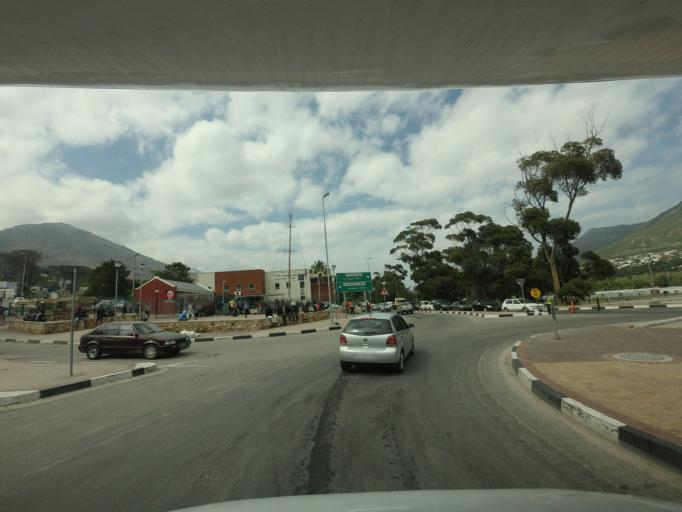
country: ZA
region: Western Cape
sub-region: City of Cape Town
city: Constantia
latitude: -34.0299
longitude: 18.3566
